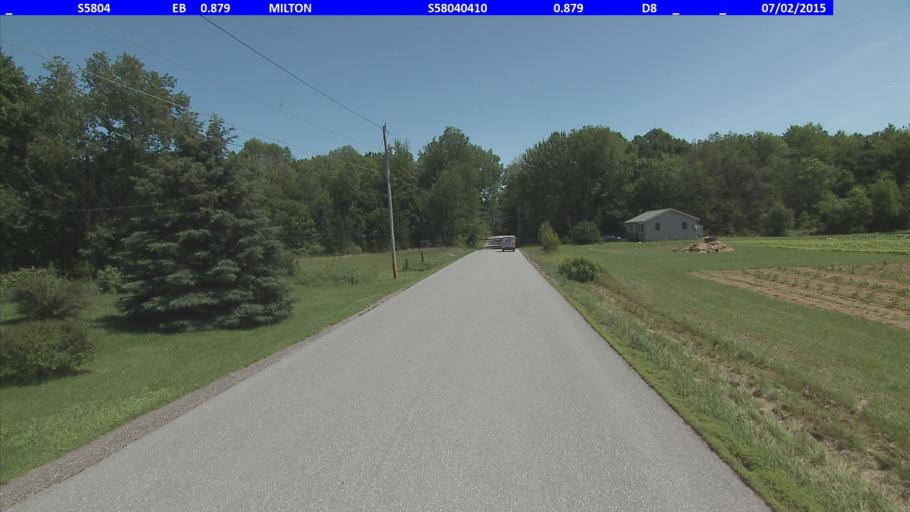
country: US
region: Vermont
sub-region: Chittenden County
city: Milton
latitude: 44.6562
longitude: -73.1557
